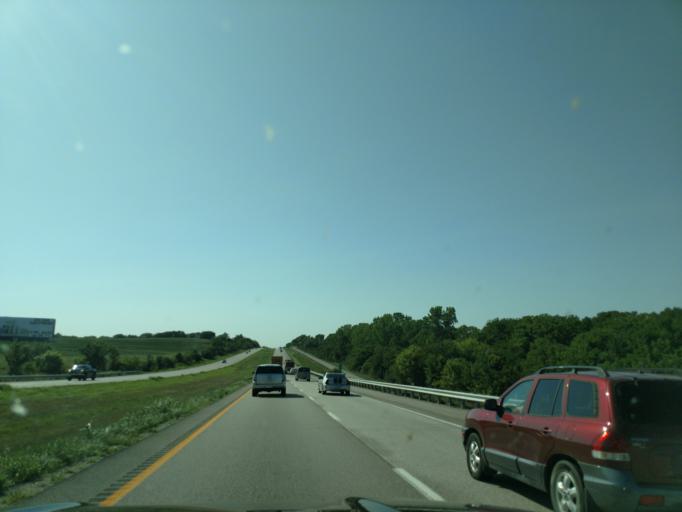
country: US
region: Missouri
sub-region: Andrew County
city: Country Club Village
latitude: 39.8726
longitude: -94.8341
